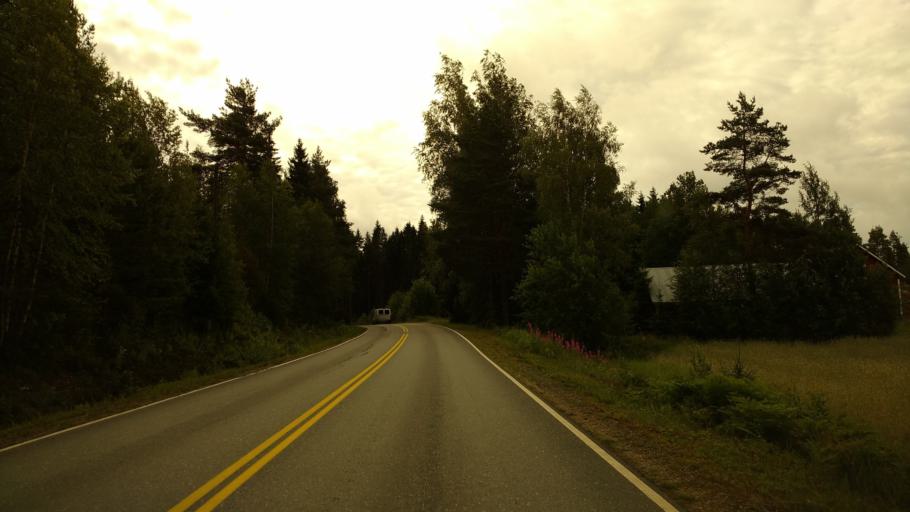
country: FI
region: Varsinais-Suomi
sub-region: Salo
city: Kuusjoki
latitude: 60.5530
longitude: 23.1577
